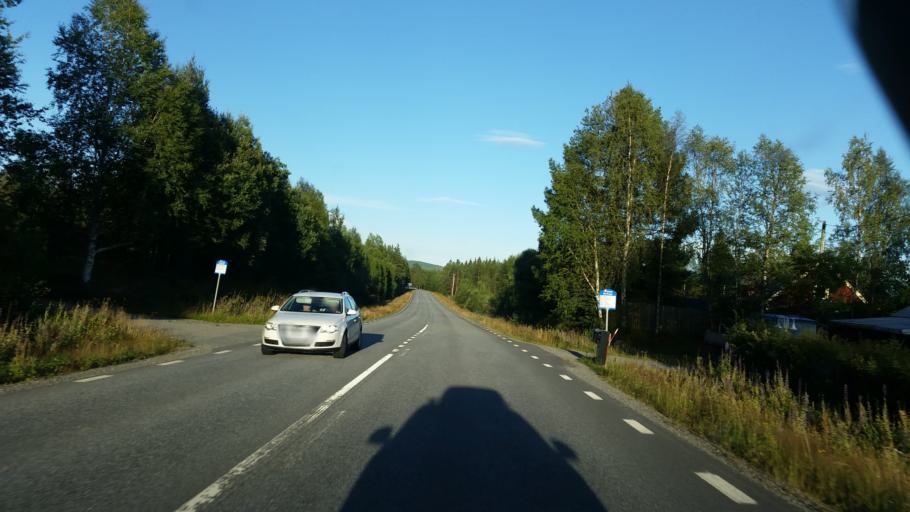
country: SE
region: Vaesterbotten
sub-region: Dorotea Kommun
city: Dorotea
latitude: 64.2544
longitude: 16.4583
